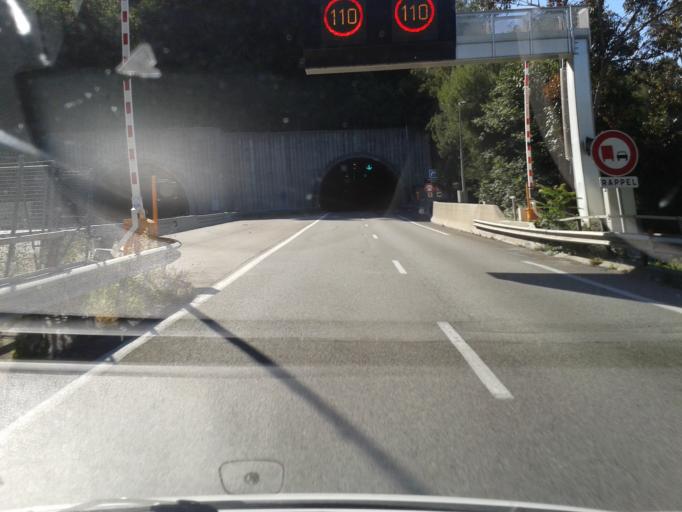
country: FR
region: Provence-Alpes-Cote d'Azur
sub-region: Departement des Alpes-Maritimes
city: Menton
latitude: 43.7959
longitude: 7.4926
